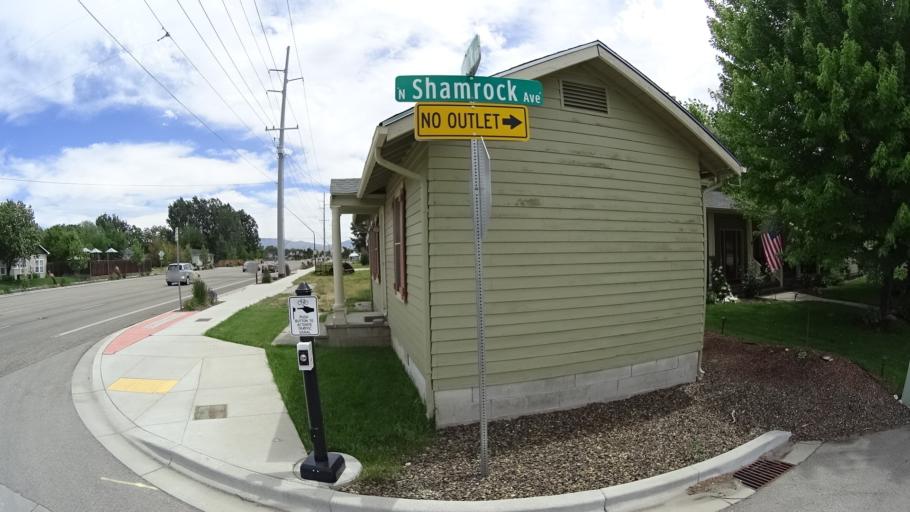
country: US
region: Idaho
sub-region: Ada County
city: Eagle
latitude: 43.6338
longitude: -116.3244
